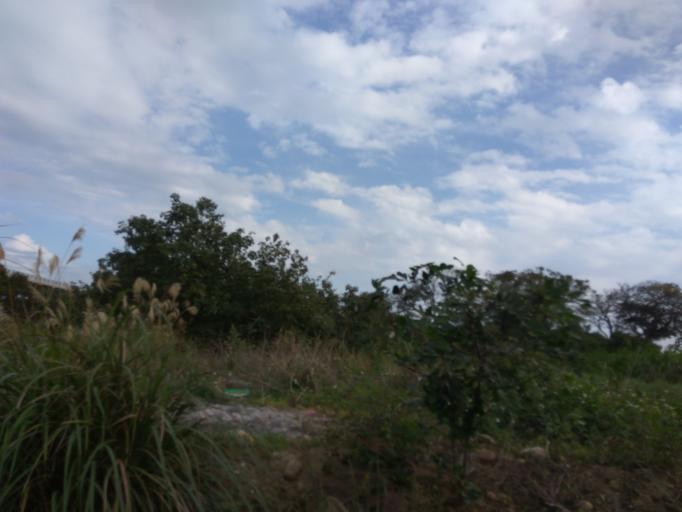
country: TW
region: Taiwan
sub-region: Hsinchu
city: Zhubei
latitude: 24.9511
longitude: 121.0003
